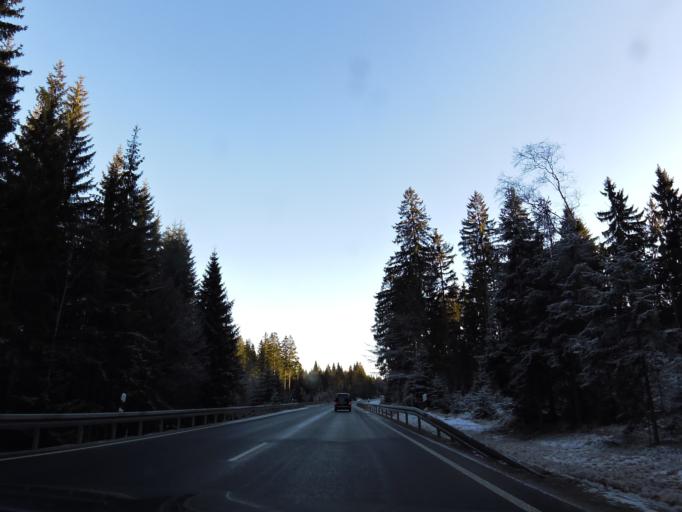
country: DE
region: Bavaria
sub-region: Upper Franconia
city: Fichtelberg
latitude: 50.0337
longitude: 11.8463
